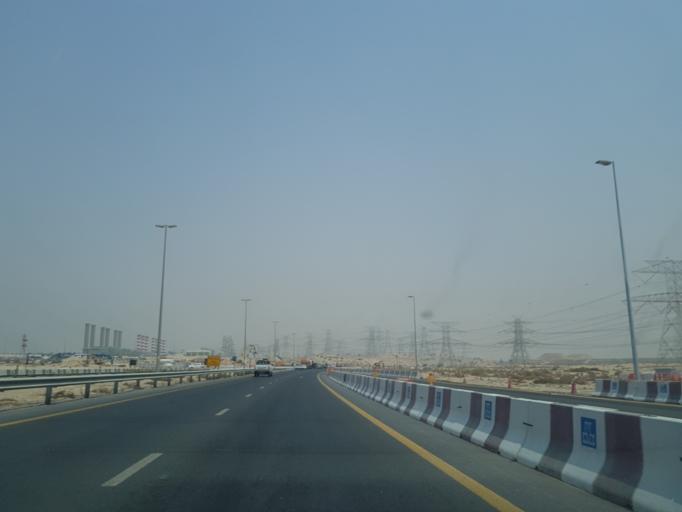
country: AE
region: Ash Shariqah
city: Sharjah
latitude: 25.1505
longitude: 55.4141
